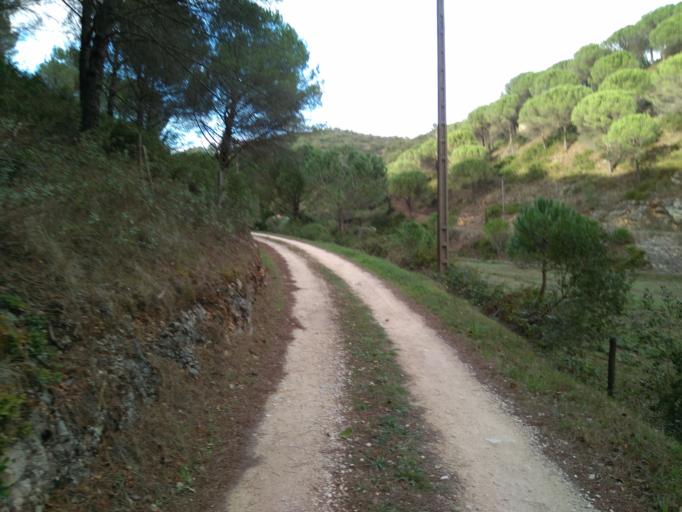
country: PT
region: Leiria
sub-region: Porto de Mos
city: Porto de Mos
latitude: 39.5919
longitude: -8.8097
